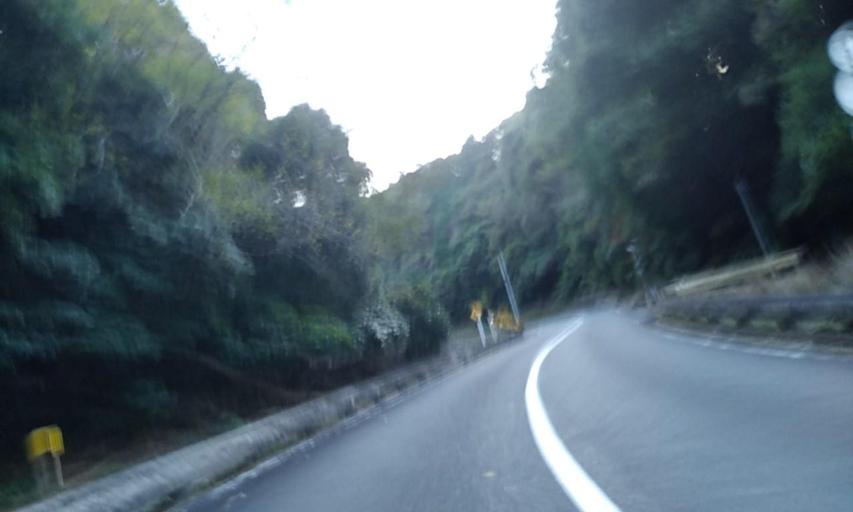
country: JP
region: Mie
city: Toba
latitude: 34.4849
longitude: 136.8355
